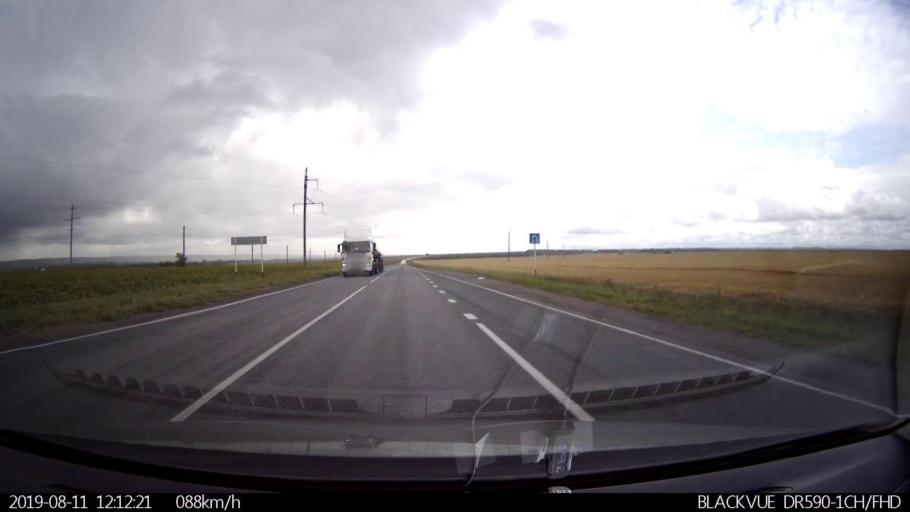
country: RU
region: Ulyanovsk
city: Silikatnyy
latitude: 53.9743
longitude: 47.9970
